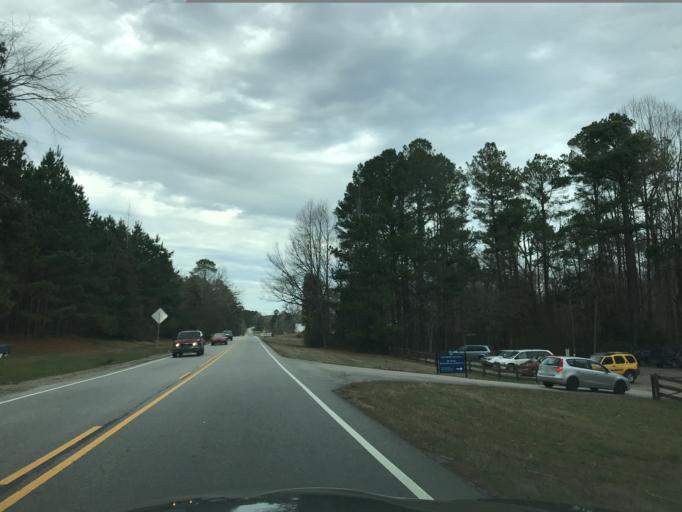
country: US
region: North Carolina
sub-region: Franklin County
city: Louisburg
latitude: 36.0235
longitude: -78.3546
